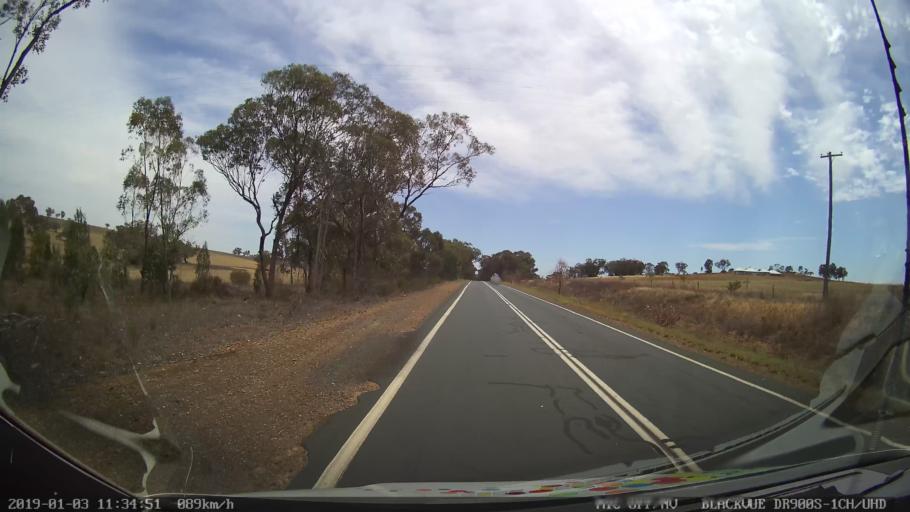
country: AU
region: New South Wales
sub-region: Weddin
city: Grenfell
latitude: -33.9297
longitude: 148.1603
